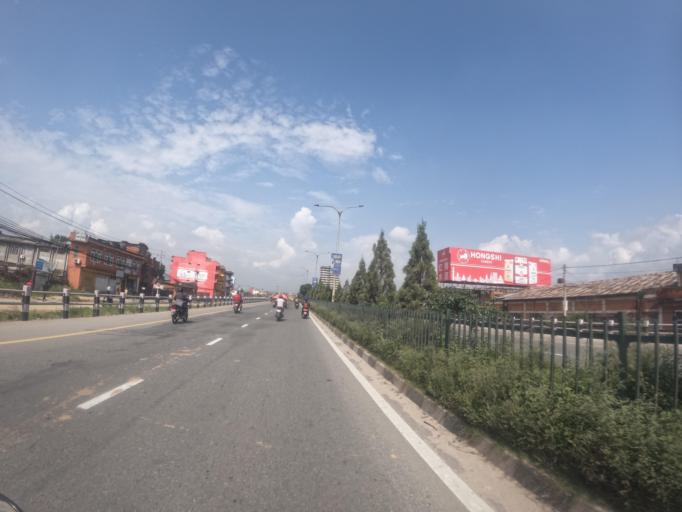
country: NP
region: Central Region
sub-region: Bagmati Zone
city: Bhaktapur
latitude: 27.6735
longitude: 85.4020
